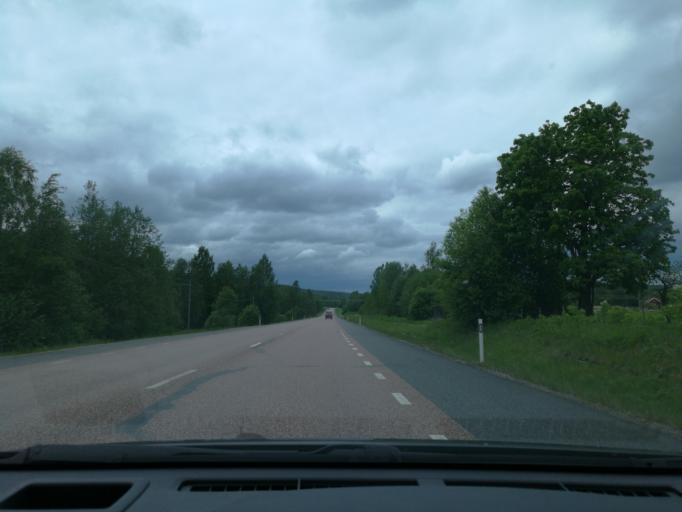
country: SE
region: Vaestmanland
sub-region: Fagersta Kommun
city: Fagersta
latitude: 59.9774
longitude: 15.6989
